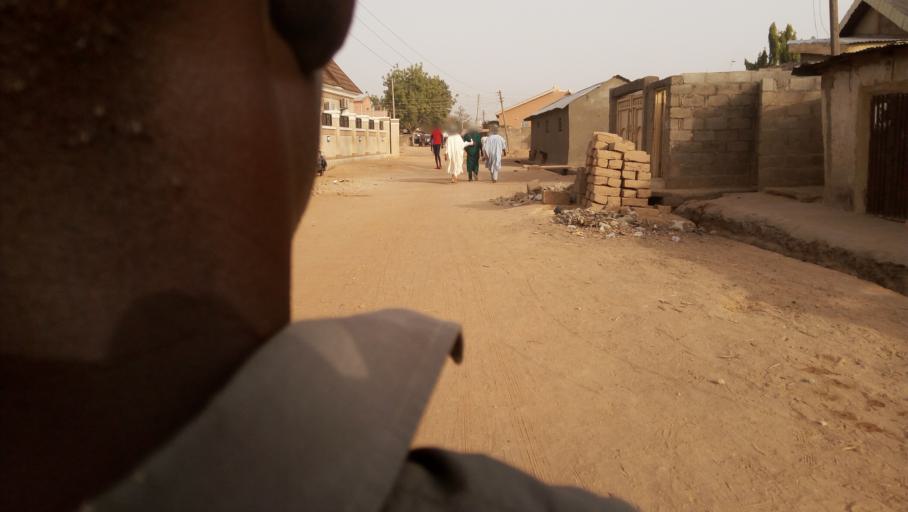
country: NG
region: Kaduna
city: Zaria
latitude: 11.1639
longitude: 7.6491
